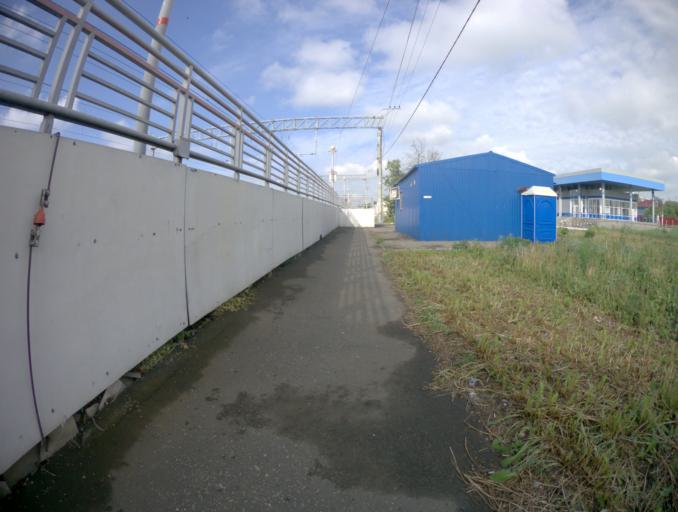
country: RU
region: Vladimir
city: Lakinsk
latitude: 56.0205
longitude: 39.9845
